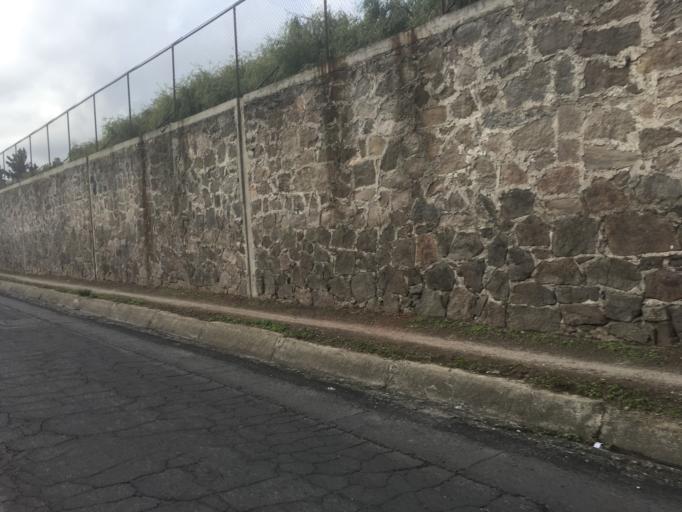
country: MX
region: Morelos
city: Metepec
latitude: 19.2588
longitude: -99.6110
